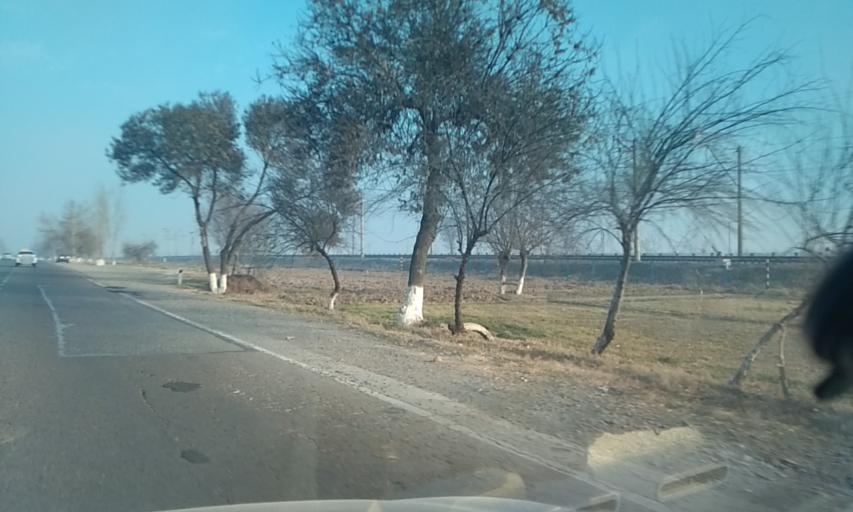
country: UZ
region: Sirdaryo
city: Sirdaryo
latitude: 40.7312
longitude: 68.6922
